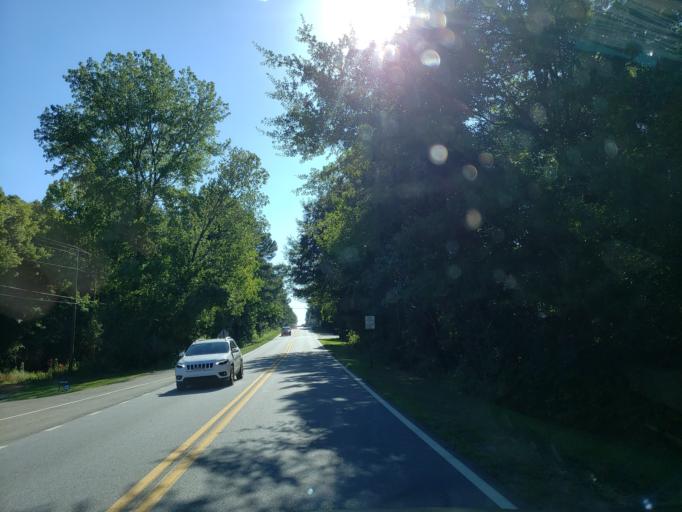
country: US
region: Georgia
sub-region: Bartow County
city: Cartersville
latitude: 34.1172
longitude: -84.8236
